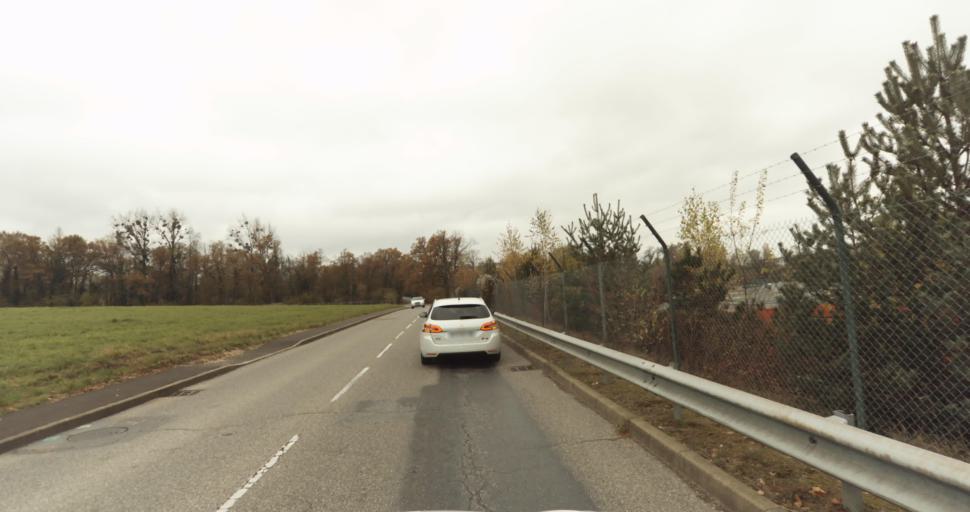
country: FR
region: Rhone-Alpes
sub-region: Departement de la Haute-Savoie
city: Seynod
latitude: 45.8753
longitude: 6.0892
